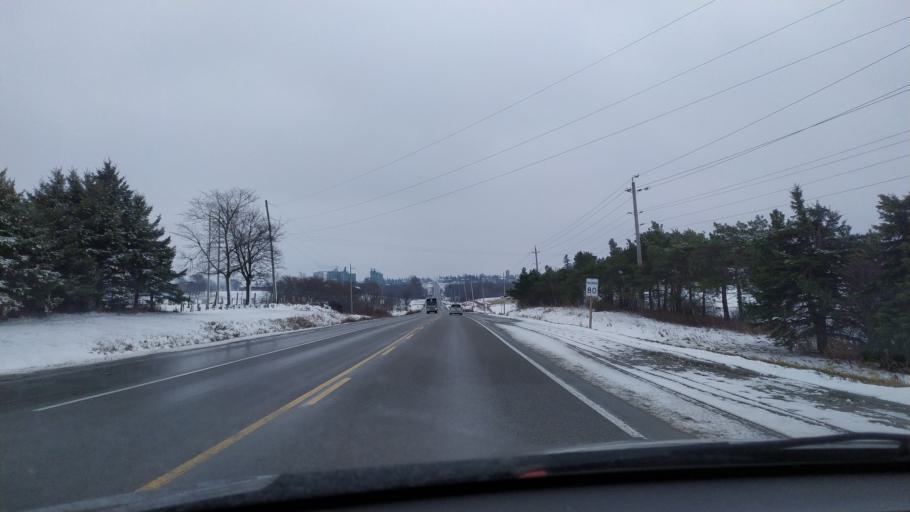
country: CA
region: Ontario
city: Waterloo
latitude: 43.6078
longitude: -80.6549
